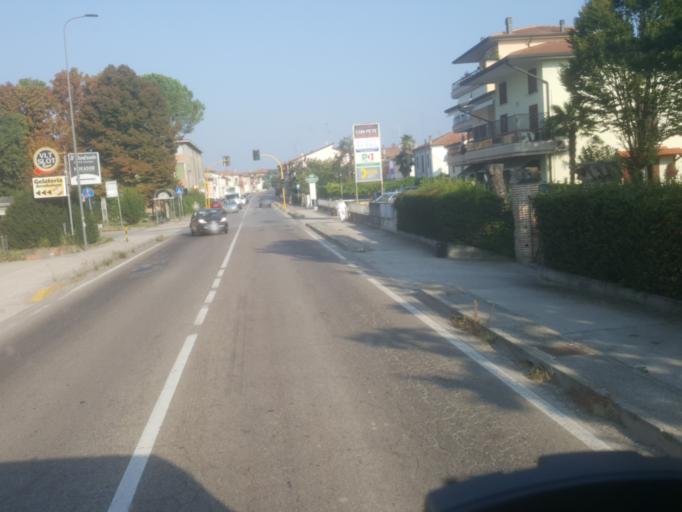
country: IT
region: Emilia-Romagna
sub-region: Provincia di Ravenna
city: Mezzano
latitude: 44.4666
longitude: 12.0873
